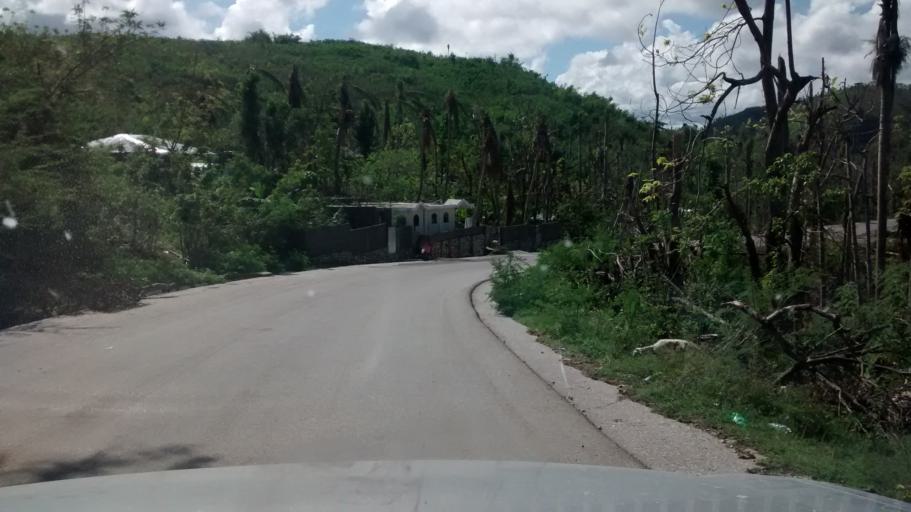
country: HT
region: Grandans
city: Jeremie
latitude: 18.6149
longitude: -74.0849
